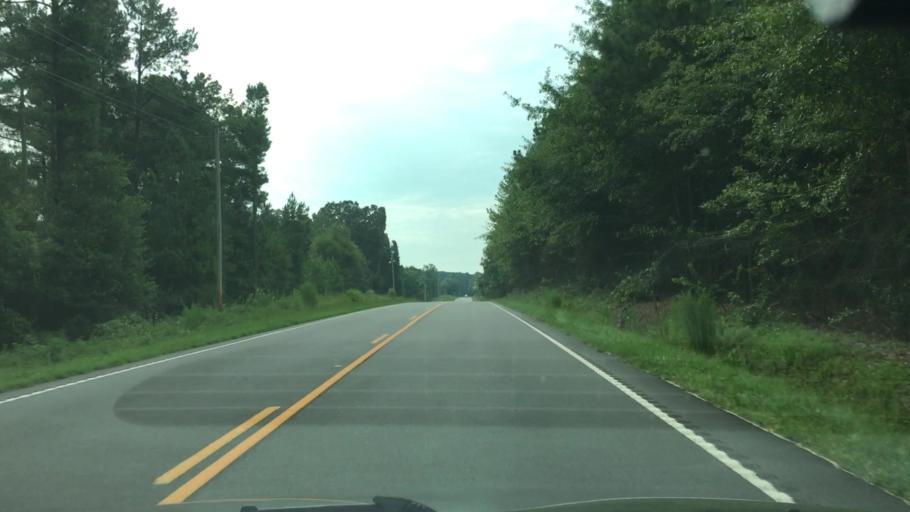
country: US
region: South Carolina
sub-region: Lexington County
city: Batesburg-Leesville
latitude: 33.7078
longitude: -81.4899
